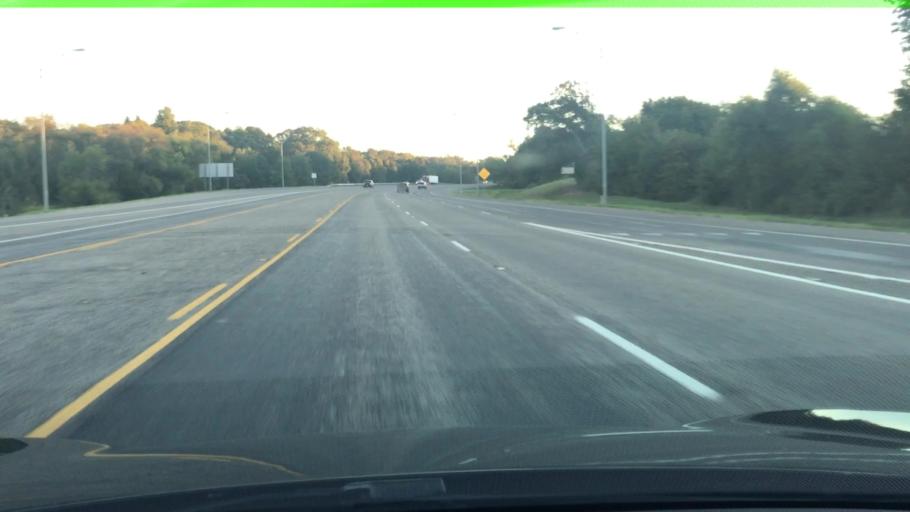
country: US
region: Texas
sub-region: Henderson County
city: Athens
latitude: 32.1919
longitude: -95.8120
